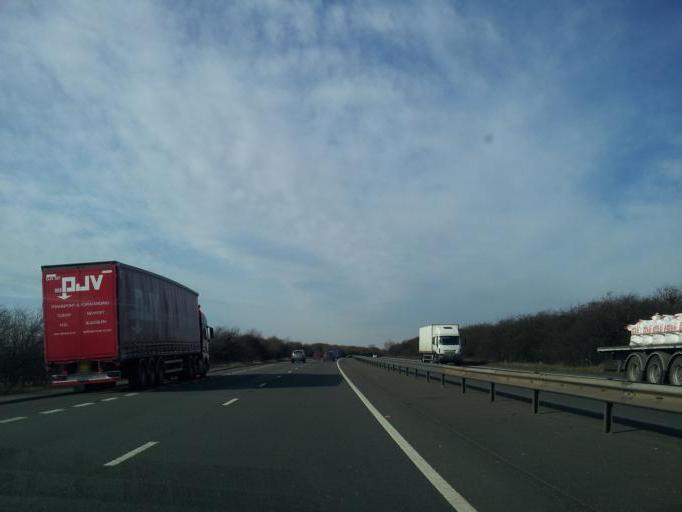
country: GB
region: England
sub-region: Lincolnshire
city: Long Bennington
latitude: 52.9864
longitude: -0.7594
